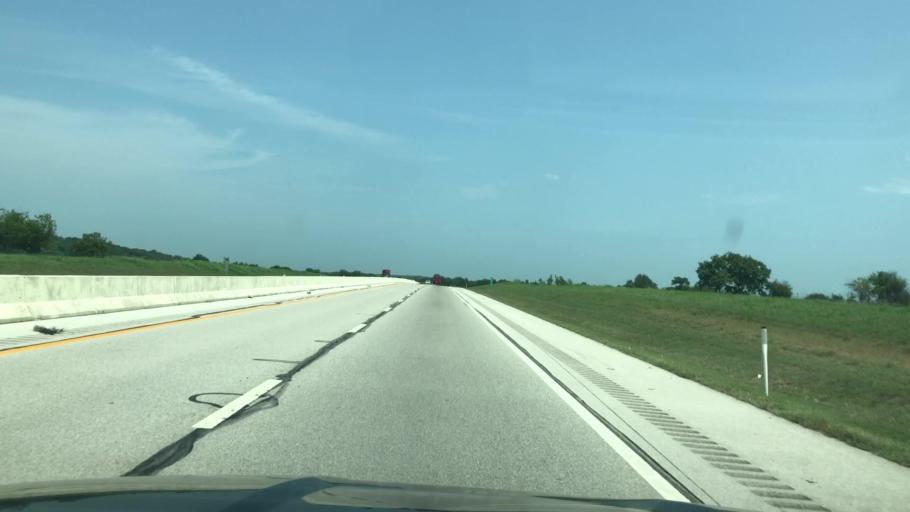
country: US
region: Oklahoma
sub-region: Rogers County
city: Justice
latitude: 36.3442
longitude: -95.4850
